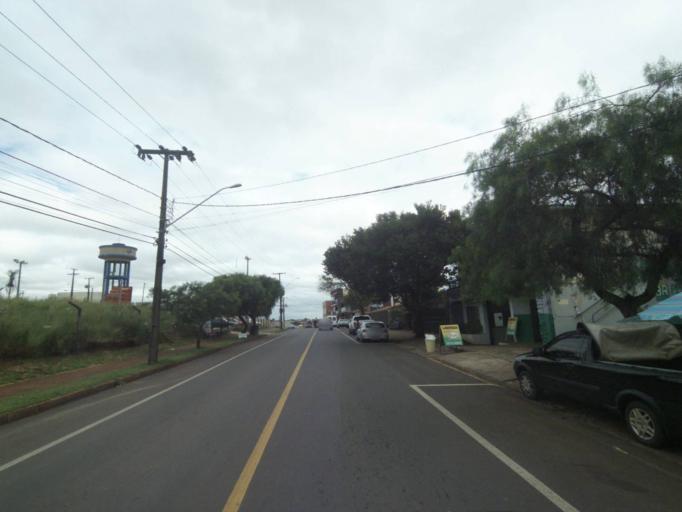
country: BR
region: Parana
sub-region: Telemaco Borba
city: Telemaco Borba
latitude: -24.3336
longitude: -50.6306
